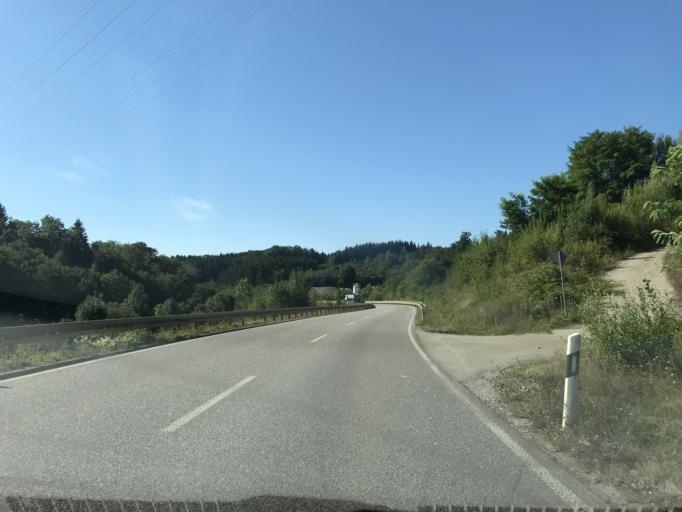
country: DE
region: Baden-Wuerttemberg
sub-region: Freiburg Region
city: Rheinfelden (Baden)
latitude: 47.5888
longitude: 7.7891
